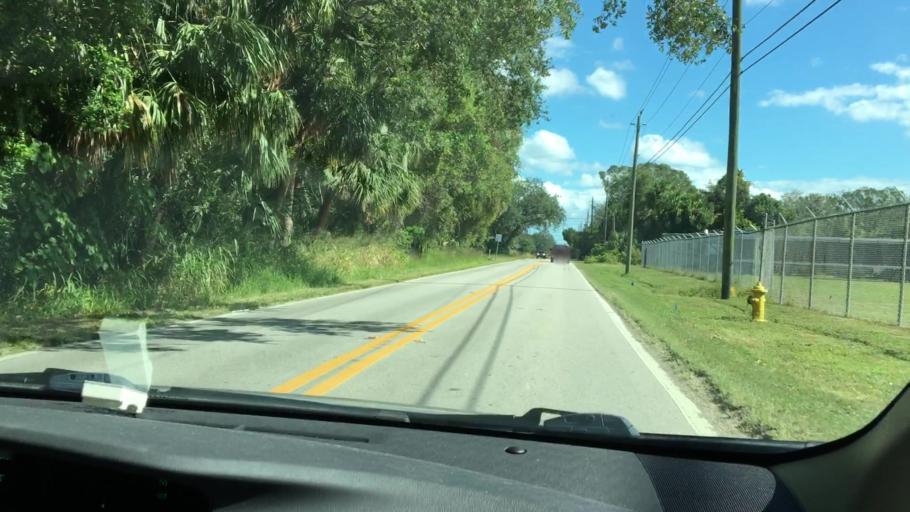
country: US
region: Florida
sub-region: Volusia County
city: DeBary
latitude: 28.8287
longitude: -81.3367
